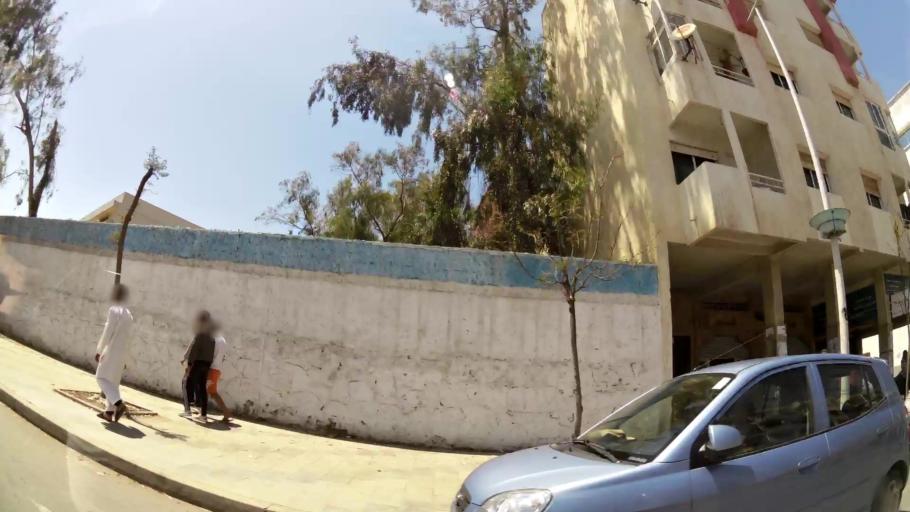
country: MA
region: Rabat-Sale-Zemmour-Zaer
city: Sale
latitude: 34.0532
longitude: -6.7957
